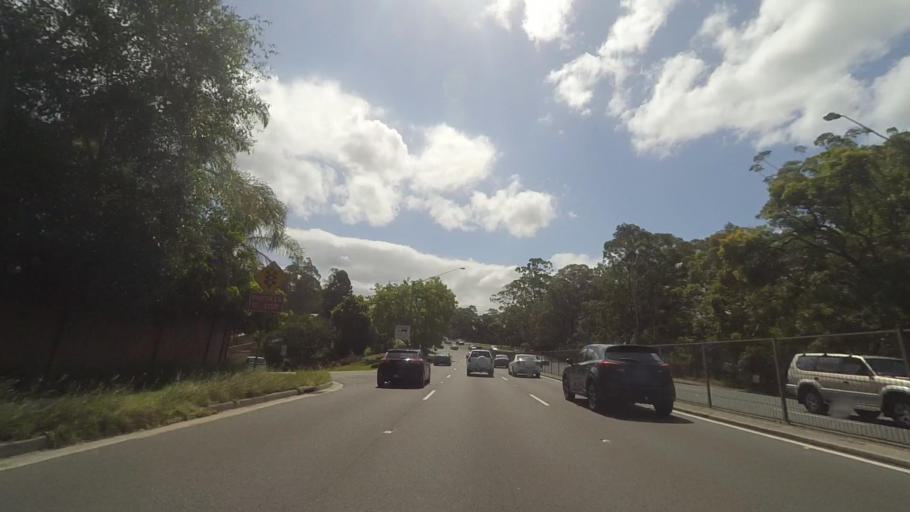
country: AU
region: New South Wales
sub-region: Ku-ring-gai
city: Normanhurst
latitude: -33.7237
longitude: 151.0930
